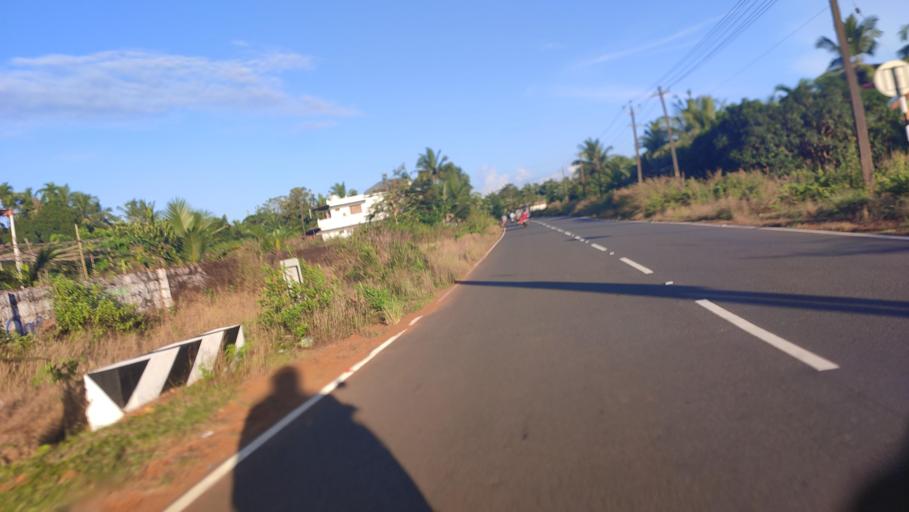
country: IN
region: Kerala
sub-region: Kasaragod District
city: Kasaragod
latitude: 12.4649
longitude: 75.0735
